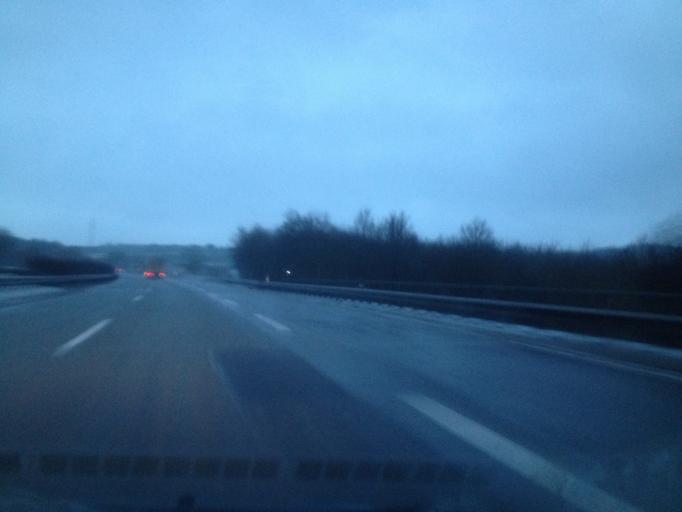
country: DE
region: Rheinland-Pfalz
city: Plaidt
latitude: 50.3791
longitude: 7.3864
